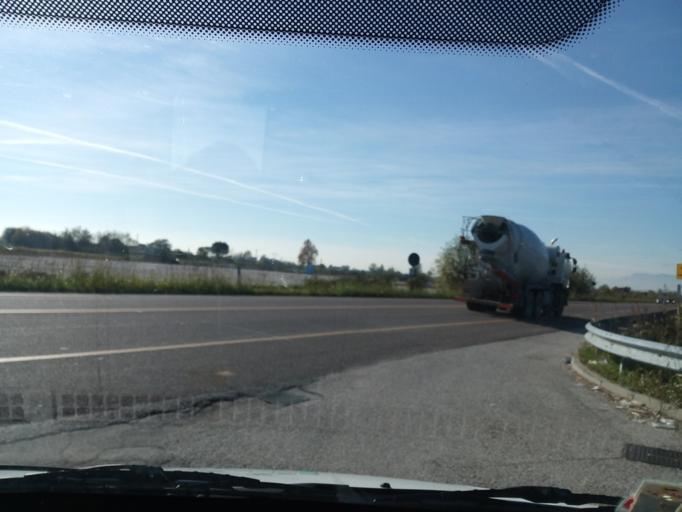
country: IT
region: Veneto
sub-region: Provincia di Vicenza
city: Bassano del Grappa
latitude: 45.7383
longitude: 11.7186
